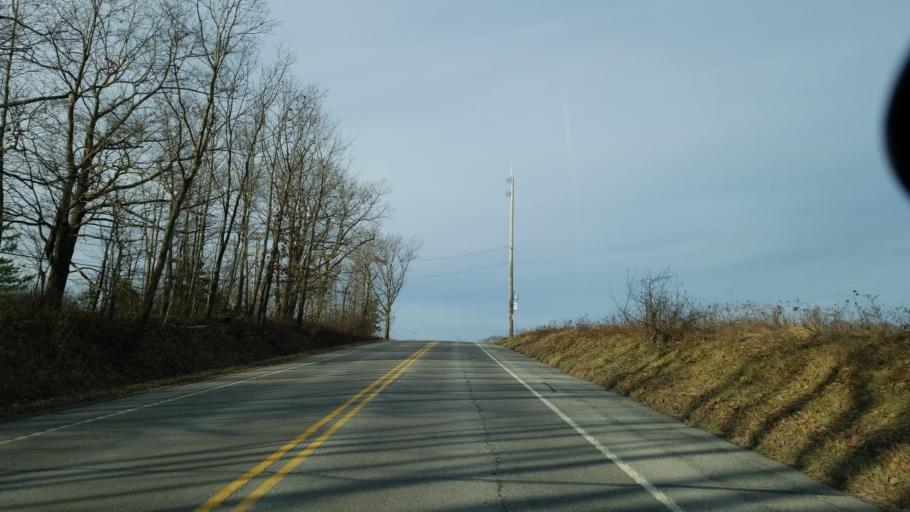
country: US
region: Pennsylvania
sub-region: Clearfield County
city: Curwensville
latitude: 41.0143
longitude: -78.6416
